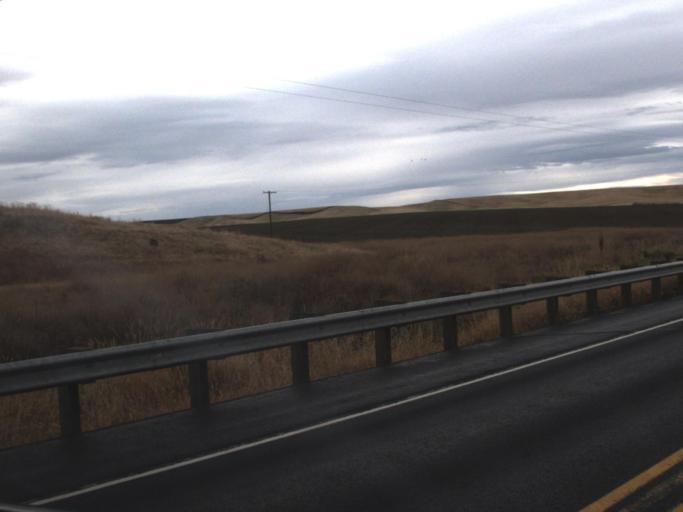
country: US
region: Washington
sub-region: Asotin County
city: Clarkston
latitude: 46.5325
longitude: -117.0857
